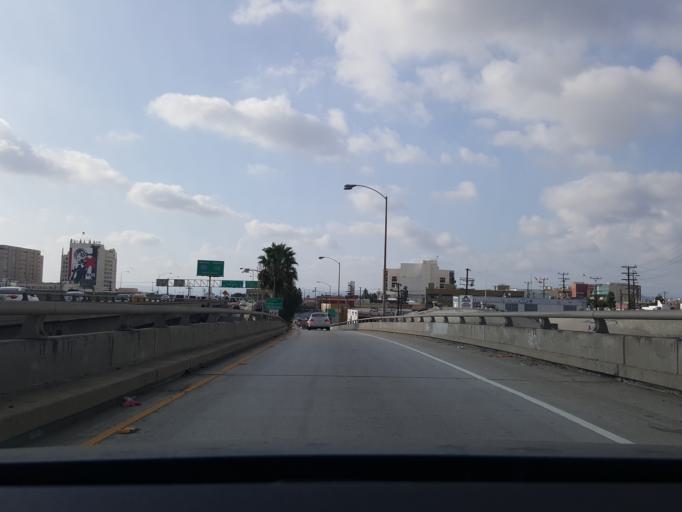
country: US
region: California
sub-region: Los Angeles County
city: Los Angeles
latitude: 34.0313
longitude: -118.2592
